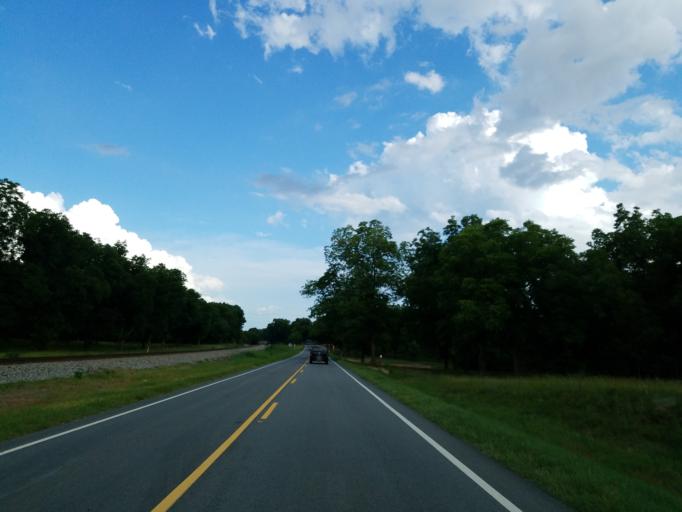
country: US
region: Georgia
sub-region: Turner County
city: Ashburn
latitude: 31.7899
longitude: -83.7058
